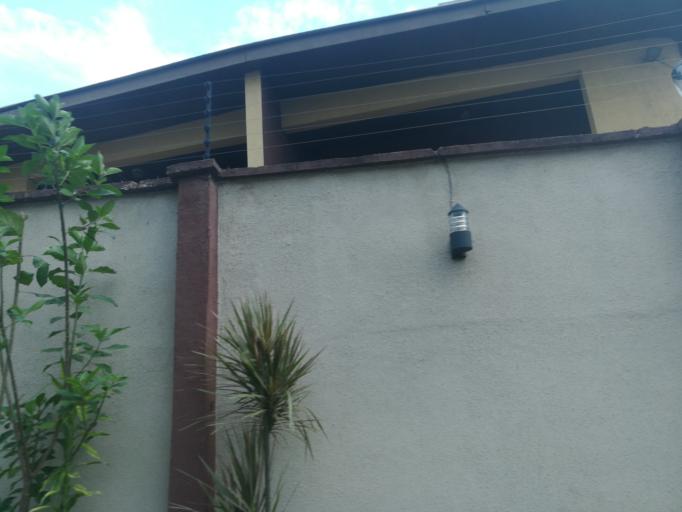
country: NG
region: Lagos
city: Ikeja
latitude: 6.6032
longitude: 3.3637
